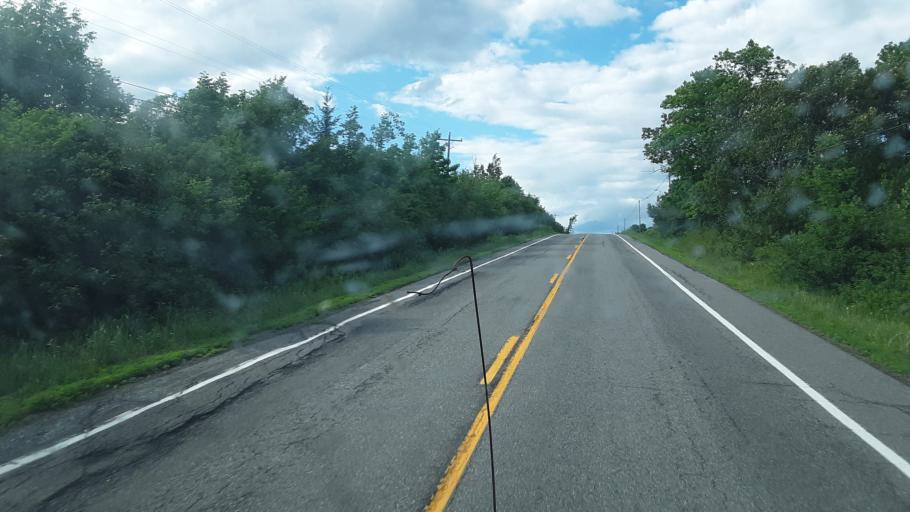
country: US
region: Maine
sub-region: Penobscot County
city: Patten
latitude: 46.0368
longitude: -68.4442
